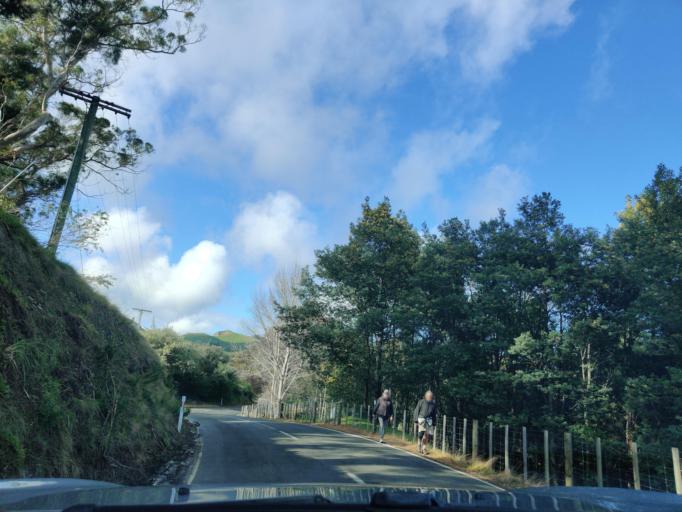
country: NZ
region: Hawke's Bay
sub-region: Hastings District
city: Hastings
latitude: -39.6783
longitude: 176.8960
